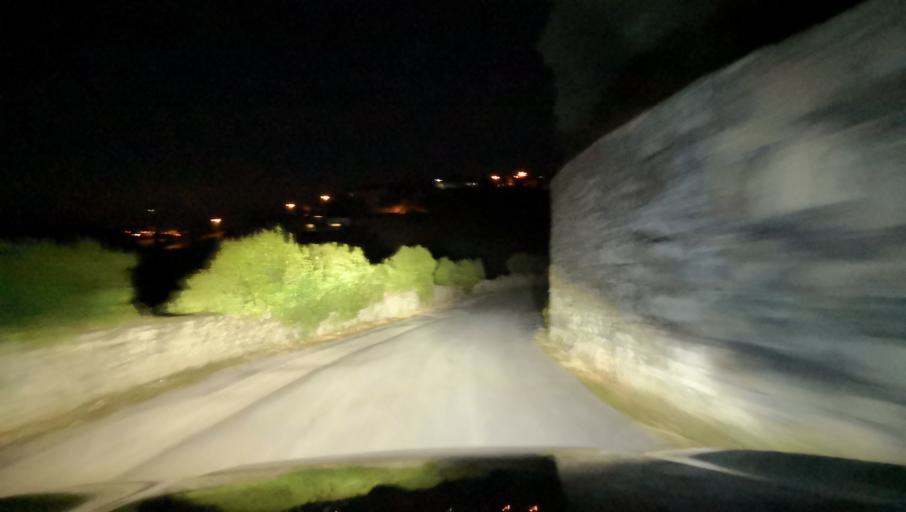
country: PT
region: Vila Real
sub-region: Peso da Regua
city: Peso da Regua
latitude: 41.1715
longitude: -7.7296
